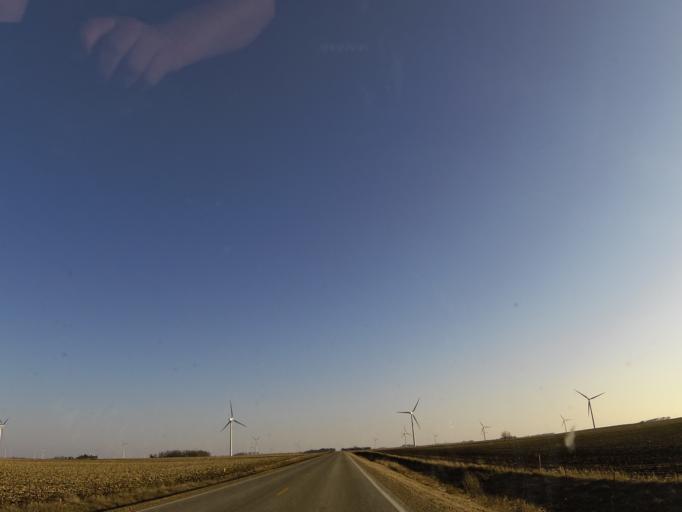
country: US
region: Iowa
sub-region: Worth County
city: Northwood
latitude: 43.4328
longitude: -93.1244
